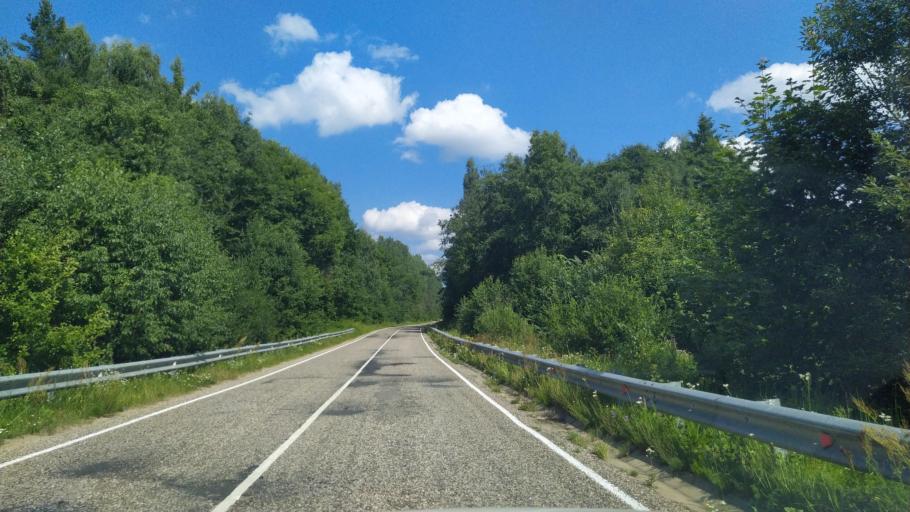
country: RU
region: Pskov
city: Pushkinskiye Gory
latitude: 57.0635
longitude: 28.9495
